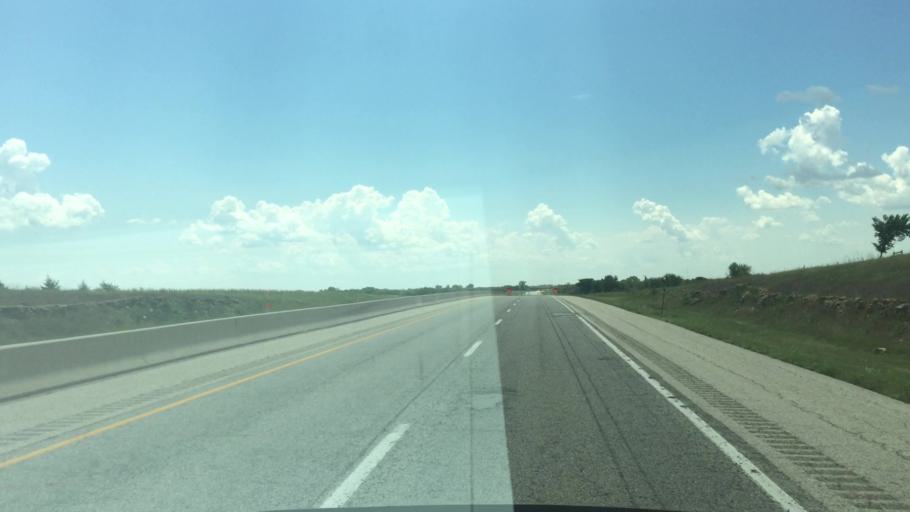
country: US
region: Kansas
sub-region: Shawnee County
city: Auburn
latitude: 38.7816
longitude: -95.9179
